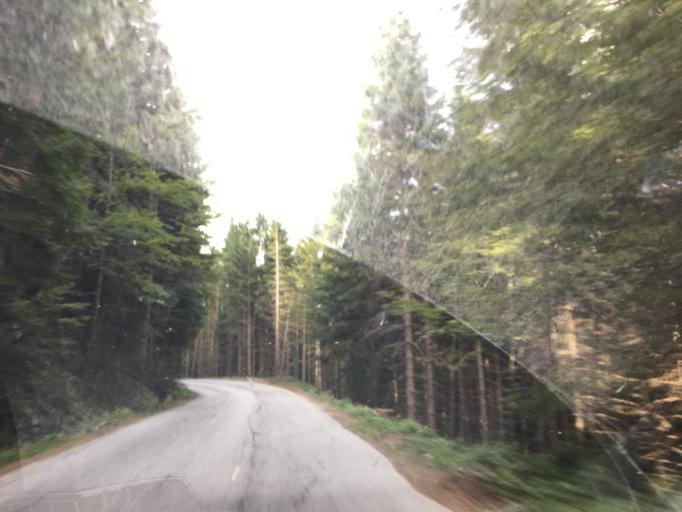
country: BG
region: Pazardzhik
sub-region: Obshtina Batak
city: Batak
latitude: 41.9204
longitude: 24.2846
